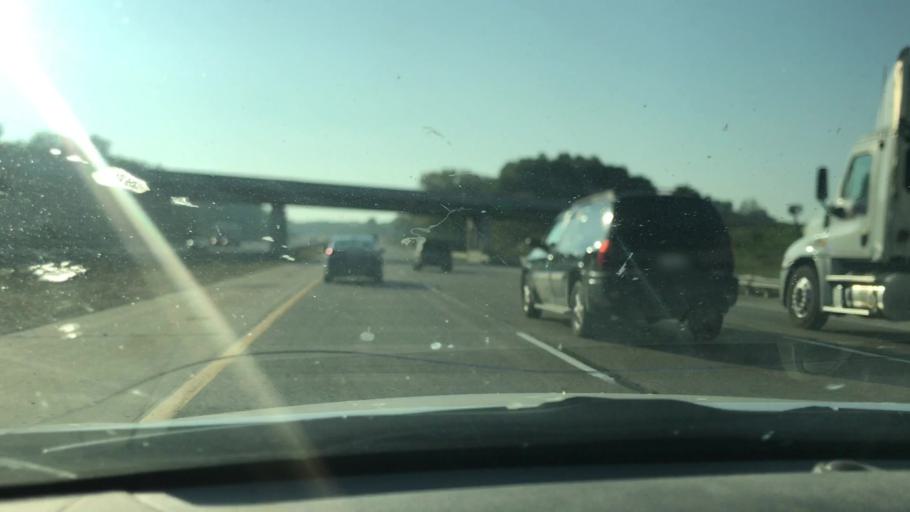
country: US
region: Michigan
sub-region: Livingston County
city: Howell
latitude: 42.5912
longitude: -83.9352
